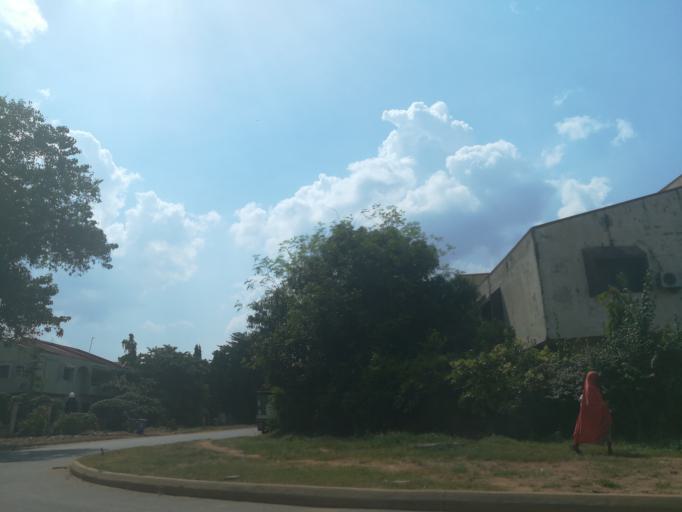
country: NG
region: Abuja Federal Capital Territory
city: Abuja
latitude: 9.0467
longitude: 7.4473
